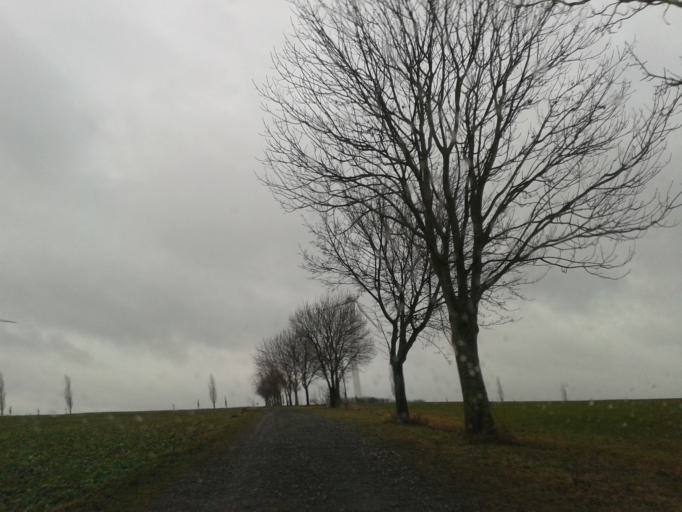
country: DE
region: Saxony
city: Neugersdorf
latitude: 50.9651
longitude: 14.6274
